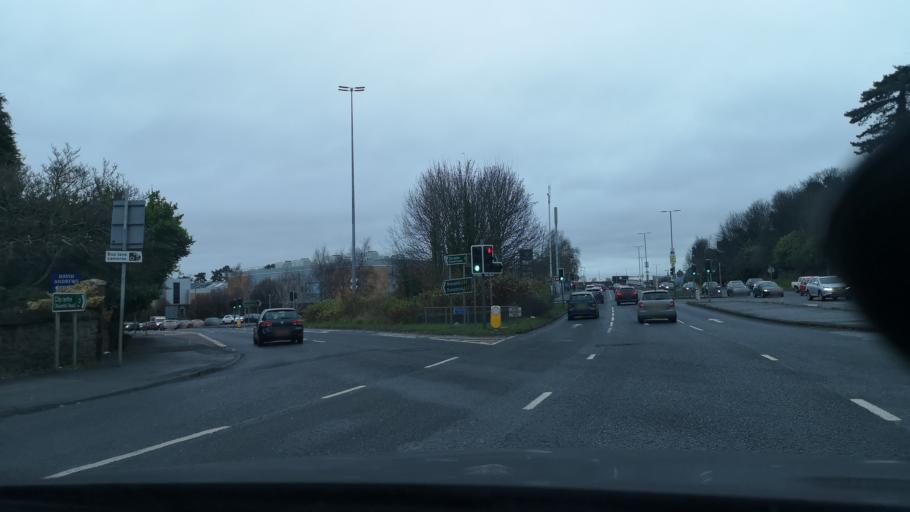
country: GB
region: Northern Ireland
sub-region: Castlereagh District
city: Castlereagh
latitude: 54.5613
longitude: -5.9098
